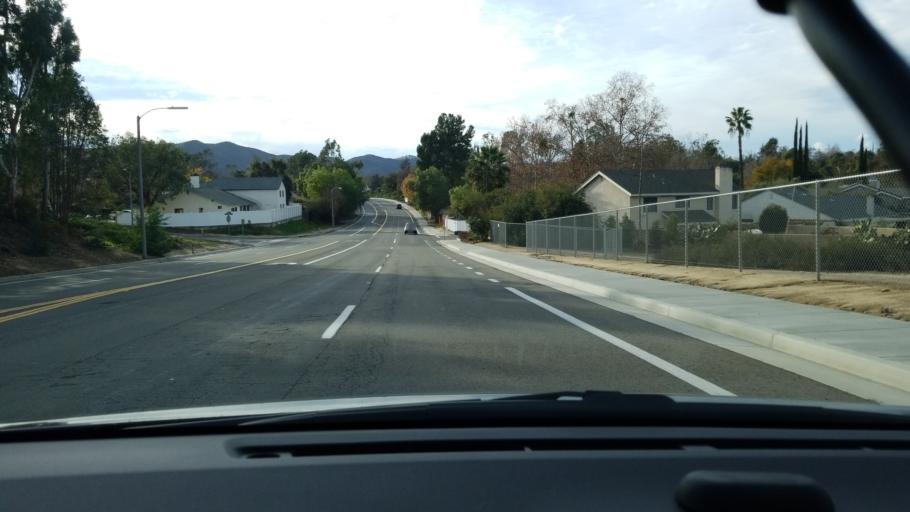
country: US
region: California
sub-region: Riverside County
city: Temecula
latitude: 33.4972
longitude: -117.1319
